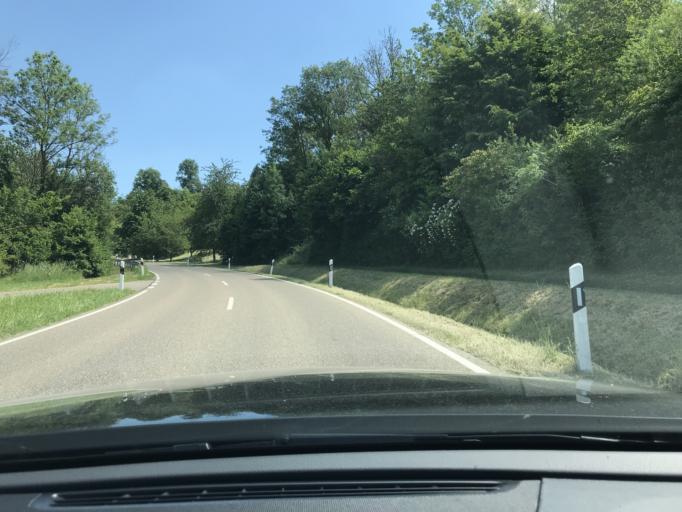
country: DE
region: Baden-Wuerttemberg
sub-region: Regierungsbezirk Stuttgart
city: Weinstadt-Endersbach
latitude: 48.7904
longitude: 9.3906
